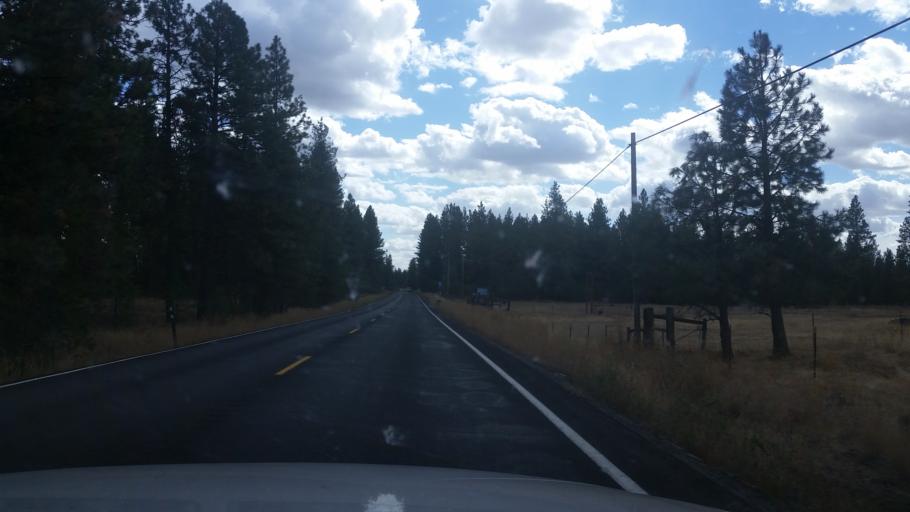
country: US
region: Washington
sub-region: Spokane County
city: Medical Lake
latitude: 47.5237
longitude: -117.7150
